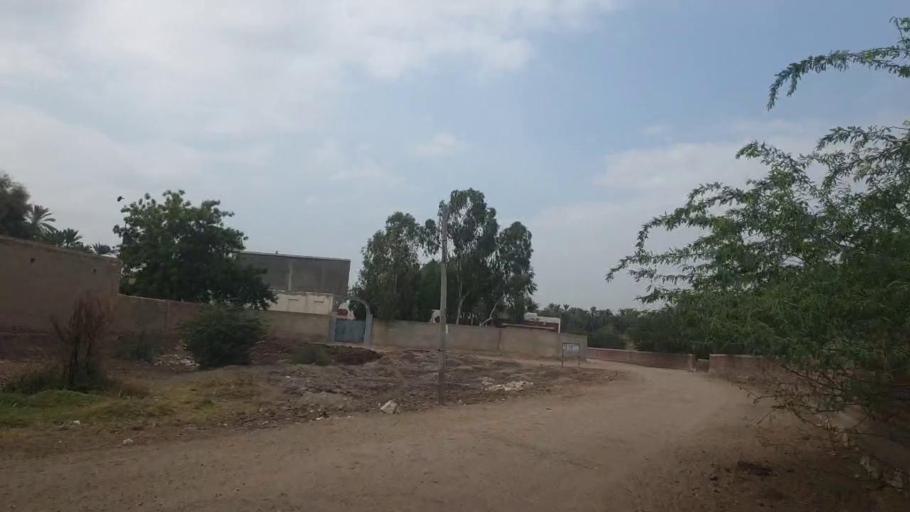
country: PK
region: Sindh
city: Sukkur
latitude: 27.6345
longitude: 68.7933
